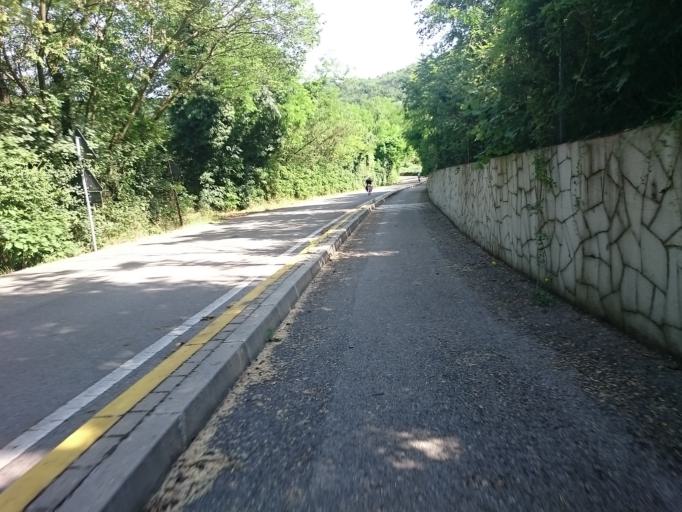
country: IT
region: Veneto
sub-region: Provincia di Padova
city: Bastia
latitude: 45.3790
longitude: 11.6699
